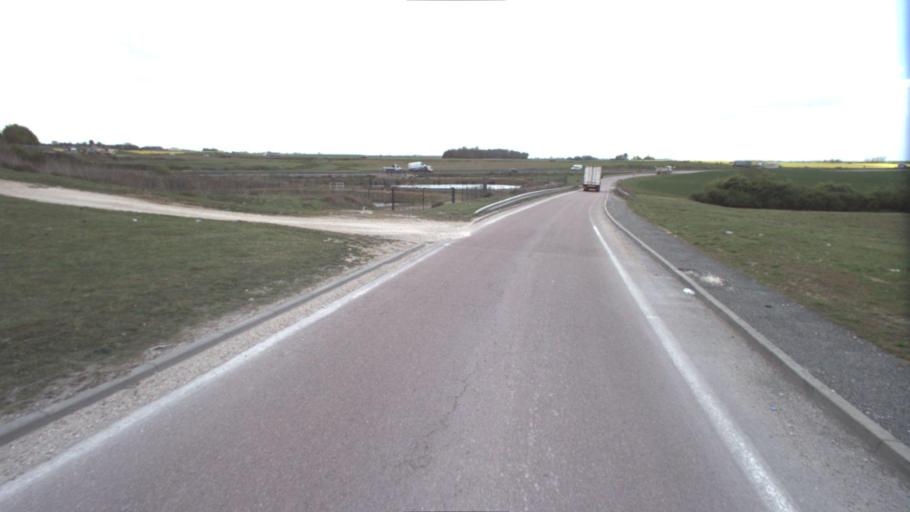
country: FR
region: Ile-de-France
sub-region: Departement de Seine-et-Marne
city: Jouy-le-Chatel
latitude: 48.6867
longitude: 3.1033
